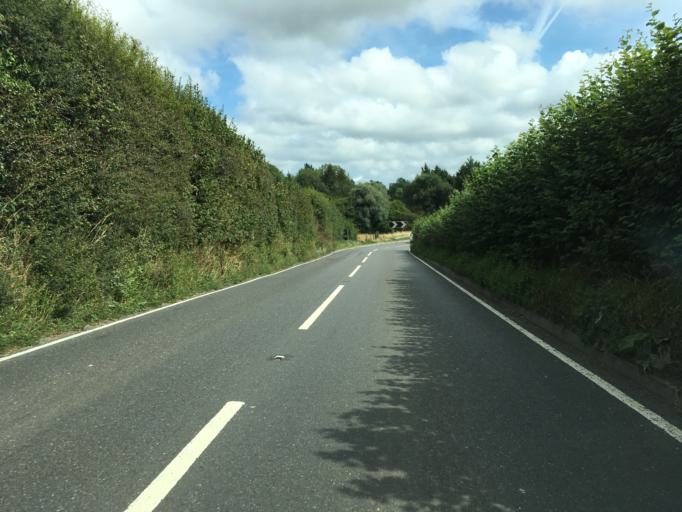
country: GB
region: England
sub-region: Kent
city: Marden
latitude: 51.1098
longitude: 0.4351
